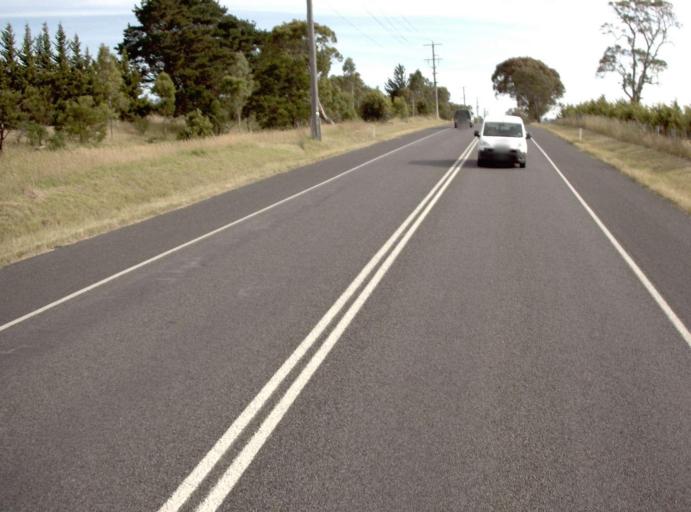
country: AU
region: Victoria
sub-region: Latrobe
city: Traralgon
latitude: -38.1765
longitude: 146.5634
